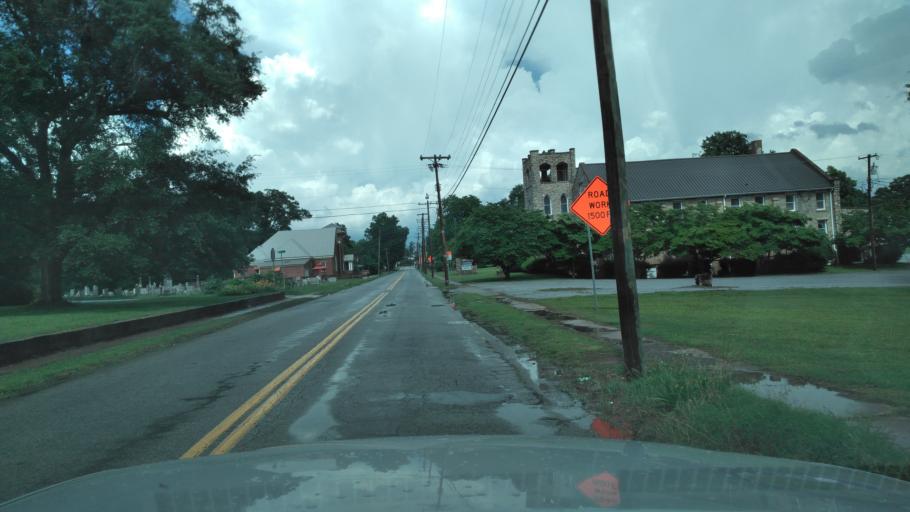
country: US
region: South Carolina
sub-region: Spartanburg County
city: Woodruff
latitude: 34.7380
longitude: -82.0417
